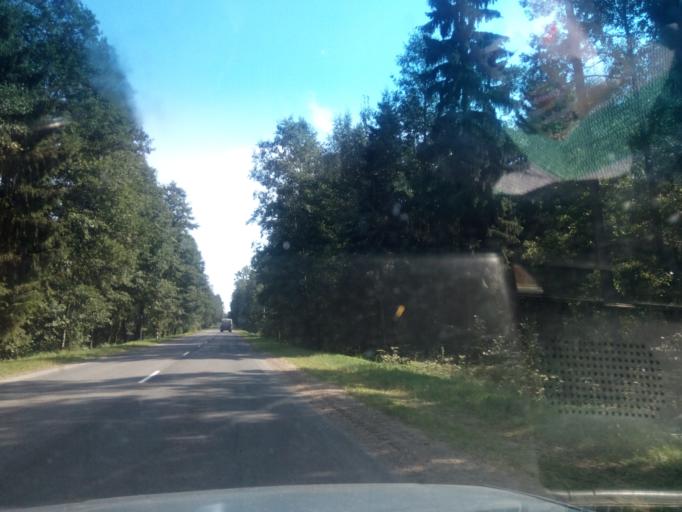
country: BY
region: Vitebsk
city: Vyerkhnyadzvinsk
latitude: 55.7965
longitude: 27.9588
